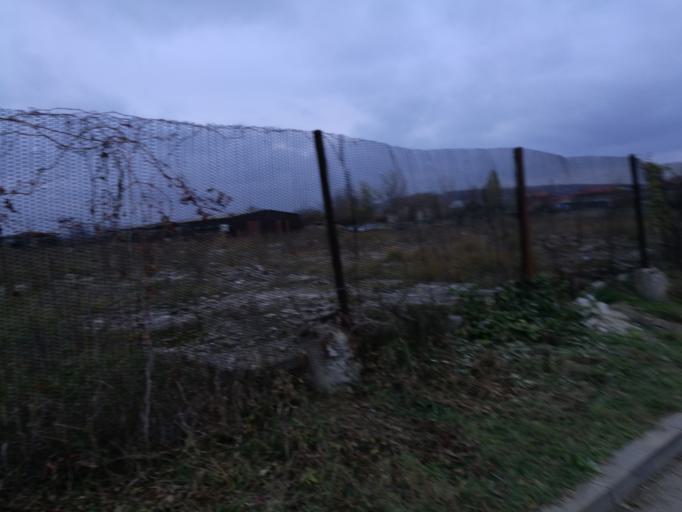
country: RO
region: Suceava
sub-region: Comuna Scheia
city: Scheia
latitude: 47.6658
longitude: 26.2655
